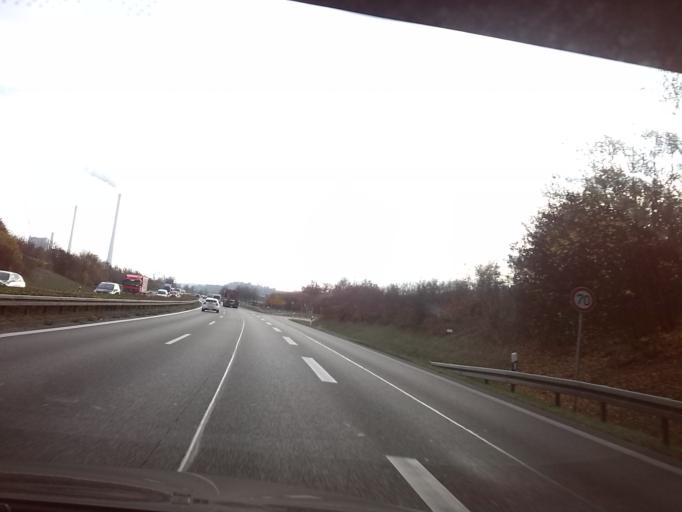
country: DE
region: Baden-Wuerttemberg
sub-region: Regierungsbezirk Stuttgart
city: Denkendorf
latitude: 48.7201
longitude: 9.3420
